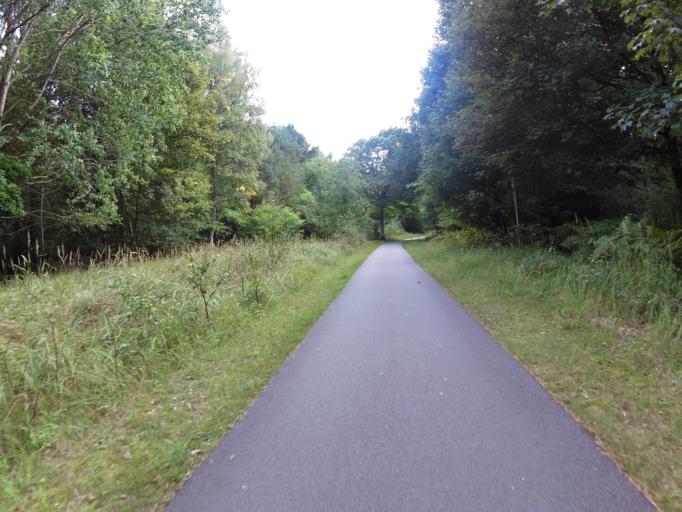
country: DE
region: Mecklenburg-Vorpommern
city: Karlshagen
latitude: 54.1343
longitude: 13.8172
